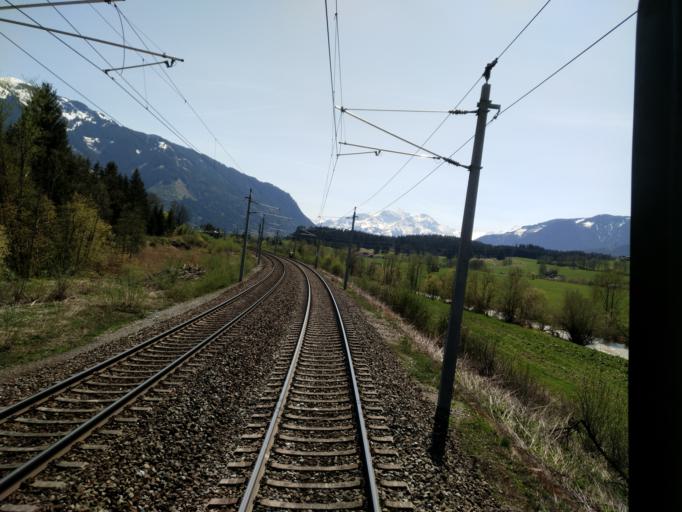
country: AT
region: Salzburg
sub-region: Politischer Bezirk Zell am See
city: Saalfelden am Steinernen Meer
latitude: 47.4126
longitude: 12.8272
